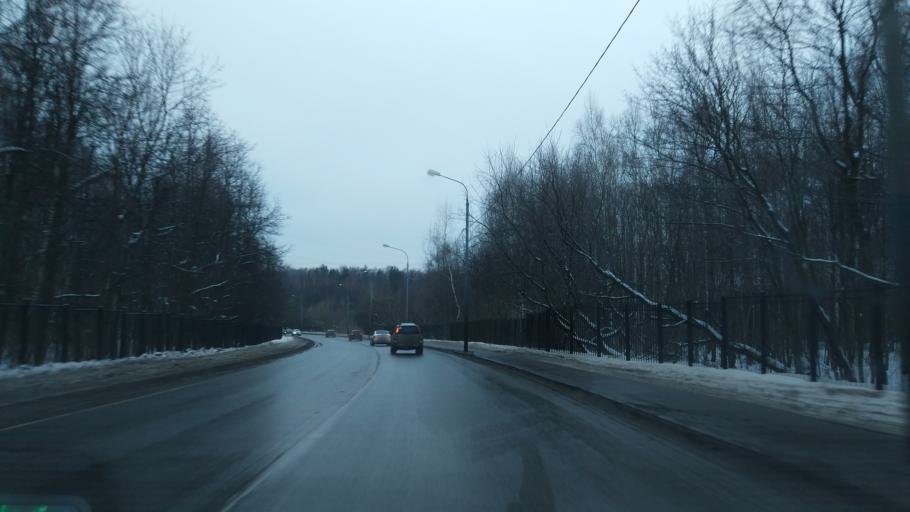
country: RU
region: Moskovskaya
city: Izmaylovo
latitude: 55.7821
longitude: 37.8207
